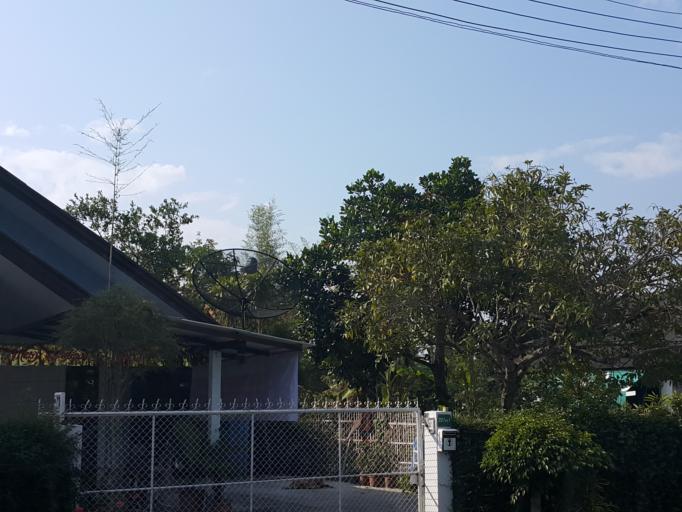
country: TH
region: Chiang Mai
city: San Sai
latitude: 18.8402
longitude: 99.1026
